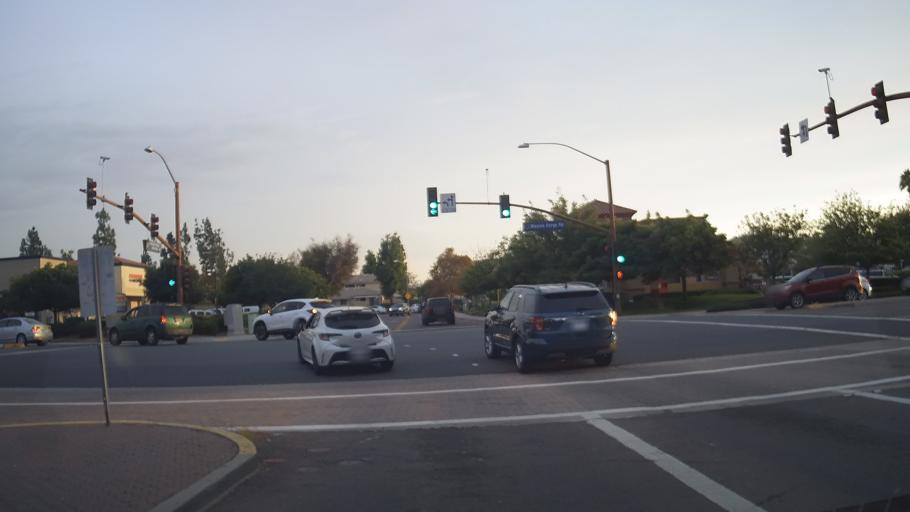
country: US
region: California
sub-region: San Diego County
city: Santee
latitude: 32.8391
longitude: -116.9796
